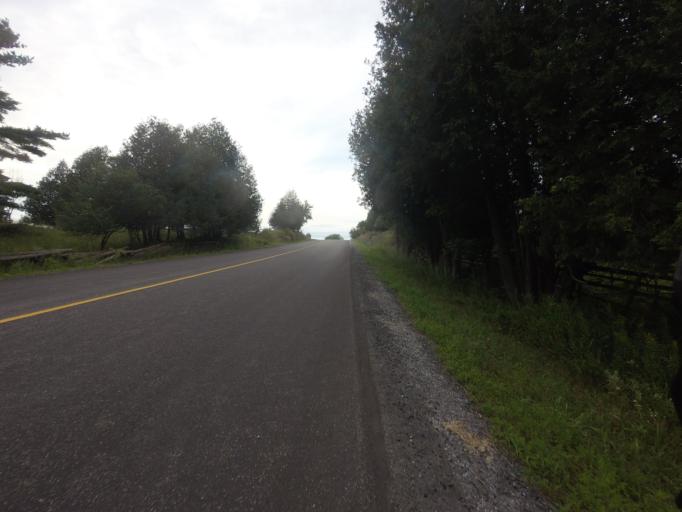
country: CA
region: Ontario
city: Perth
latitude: 45.0766
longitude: -76.3929
